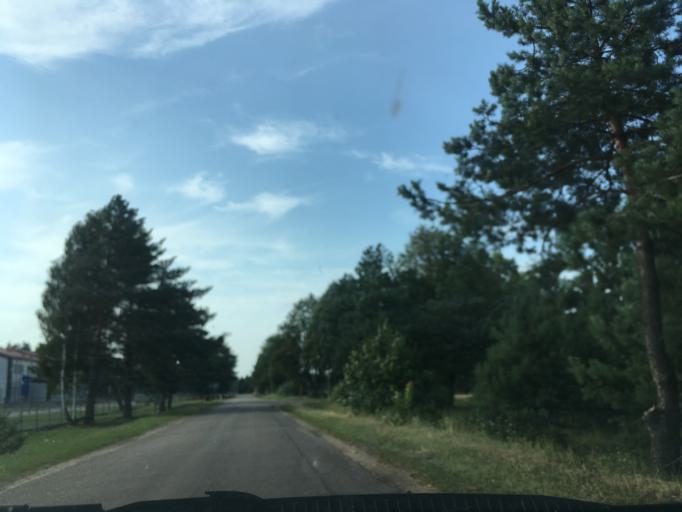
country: PL
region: Podlasie
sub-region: Powiat hajnowski
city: Bialowieza
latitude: 52.9022
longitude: 23.8294
